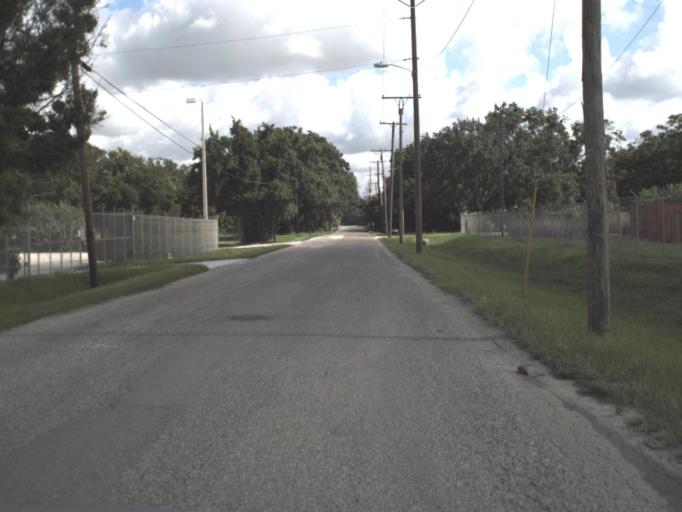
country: US
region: Florida
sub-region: Hillsborough County
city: East Lake-Orient Park
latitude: 27.9620
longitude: -82.3853
